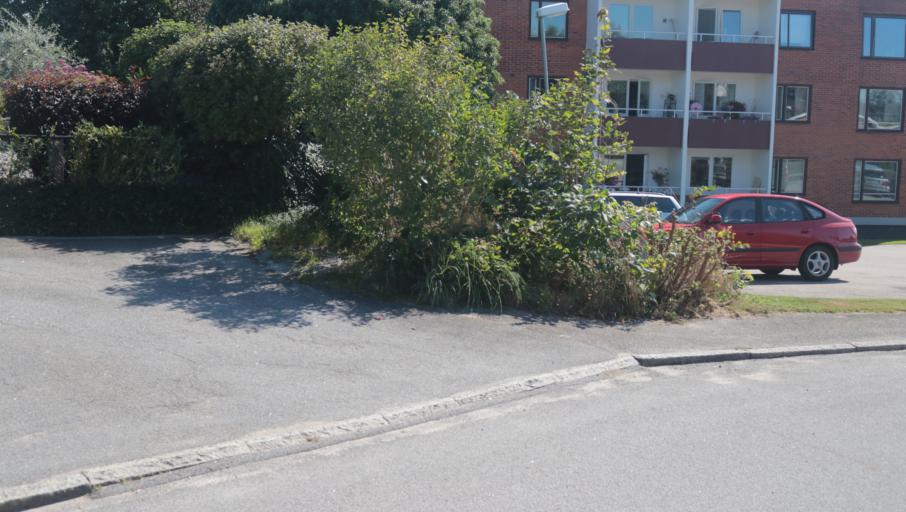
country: SE
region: Blekinge
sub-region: Karlshamns Kommun
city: Karlshamn
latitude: 56.2028
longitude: 14.8328
